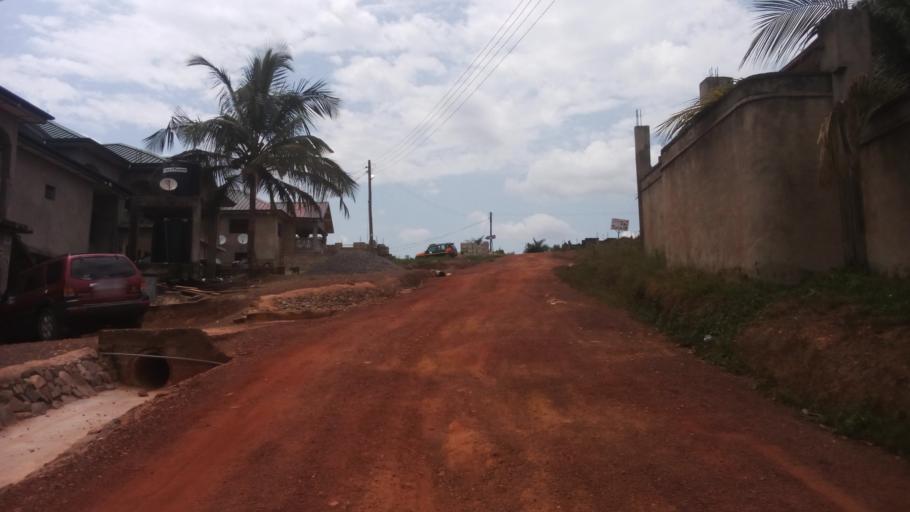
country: GH
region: Western
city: Tarkwa
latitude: 5.3047
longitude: -2.0044
